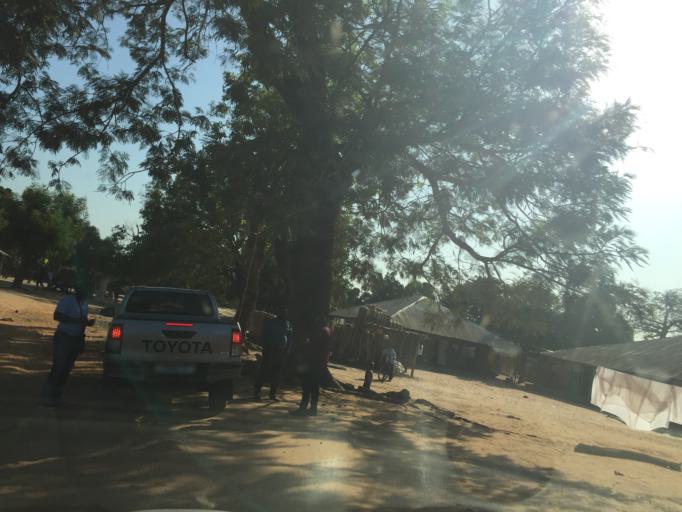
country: GW
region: Oio
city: Farim
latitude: 12.4524
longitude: -15.3082
